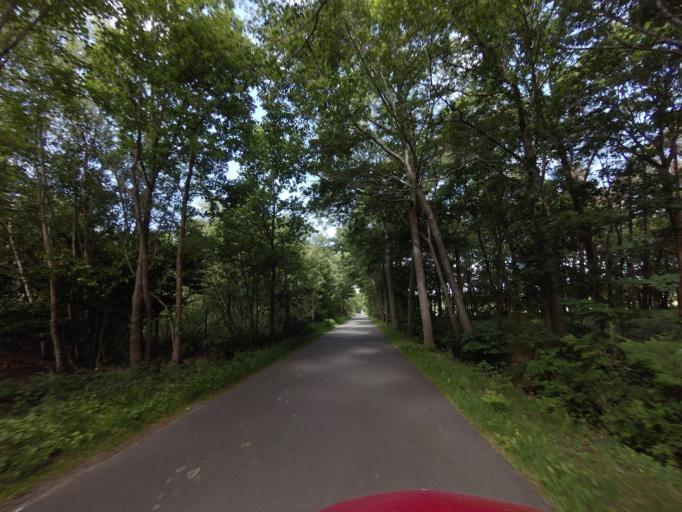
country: BE
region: Flanders
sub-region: Provincie Oost-Vlaanderen
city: Knesselare
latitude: 51.1627
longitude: 3.4261
